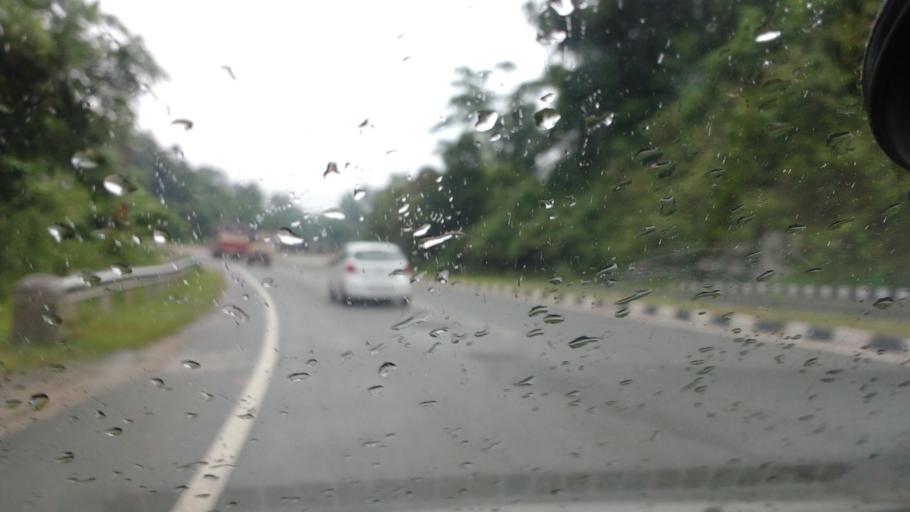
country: IN
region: Meghalaya
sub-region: Ri-Bhoi
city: Nongpoh
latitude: 25.8277
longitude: 91.8743
